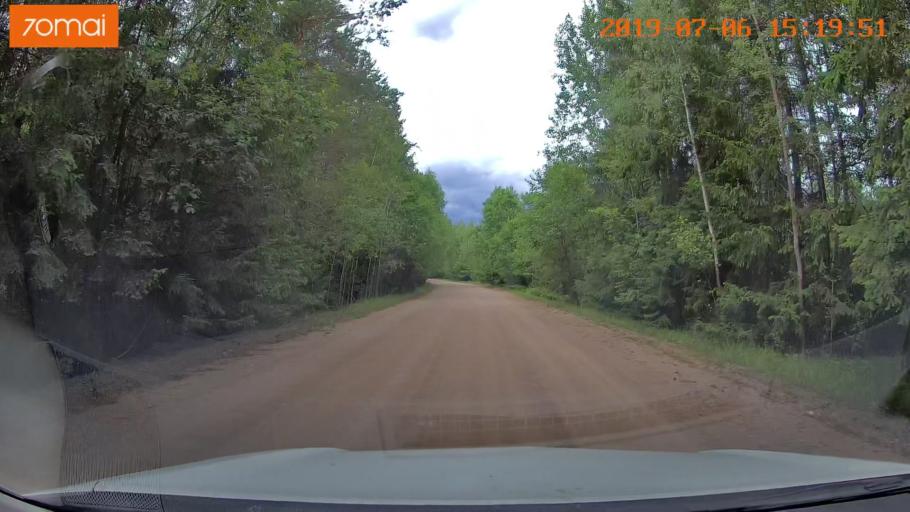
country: BY
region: Minsk
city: Valozhyn
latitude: 54.0016
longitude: 26.6434
